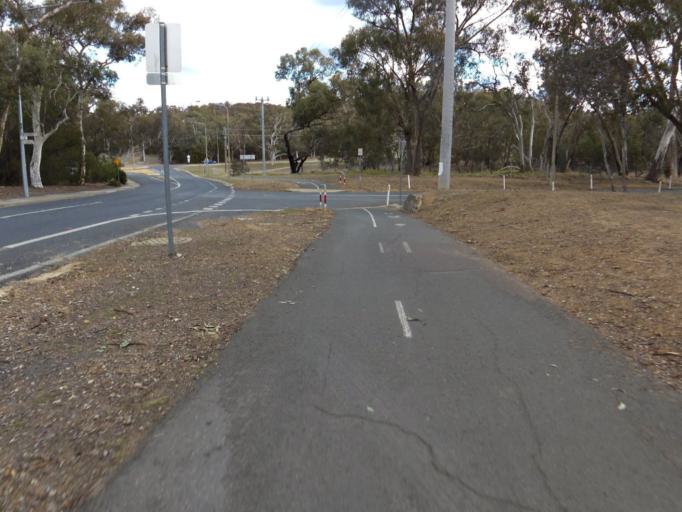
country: AU
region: Australian Capital Territory
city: Acton
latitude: -35.2573
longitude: 149.1096
